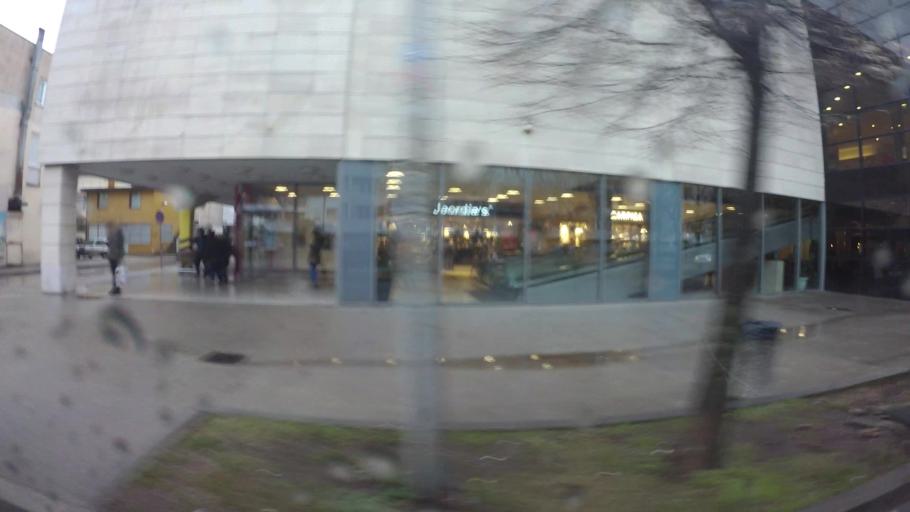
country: BA
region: Federation of Bosnia and Herzegovina
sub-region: Hercegovacko-Bosanski Kanton
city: Mostar
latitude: 43.3465
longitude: 17.7984
